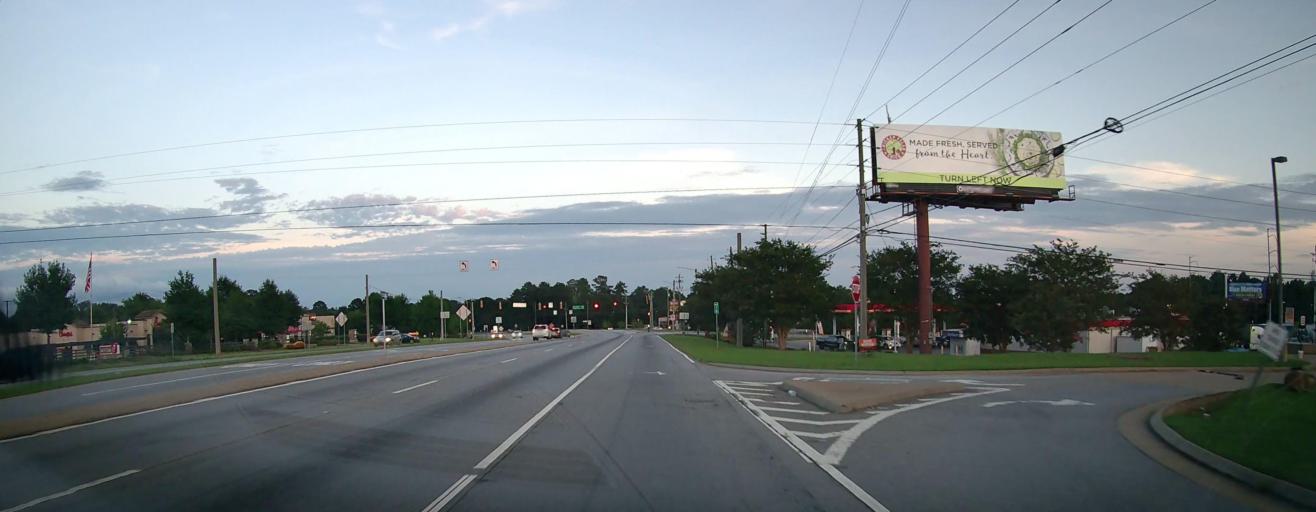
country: US
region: Georgia
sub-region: Muscogee County
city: Columbus
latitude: 32.5394
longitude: -84.8705
